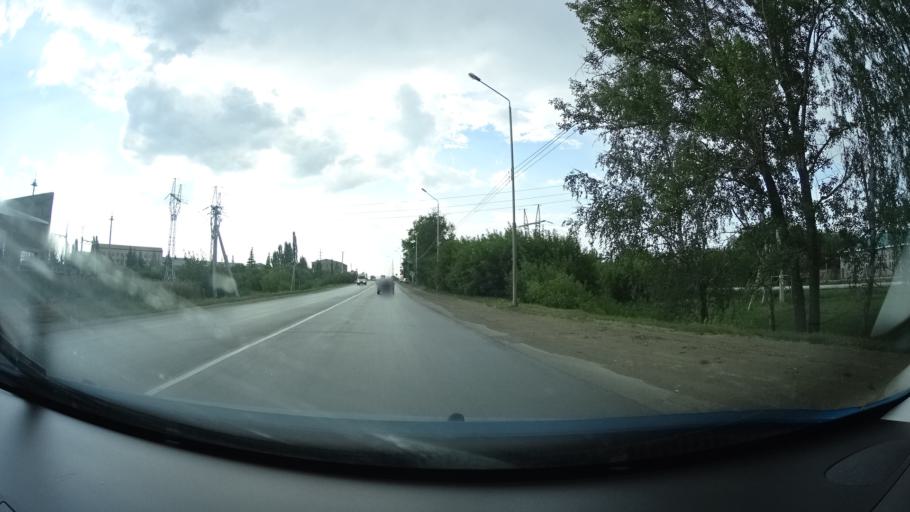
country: RU
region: Bashkortostan
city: Oktyabr'skiy
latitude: 54.4928
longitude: 53.4517
